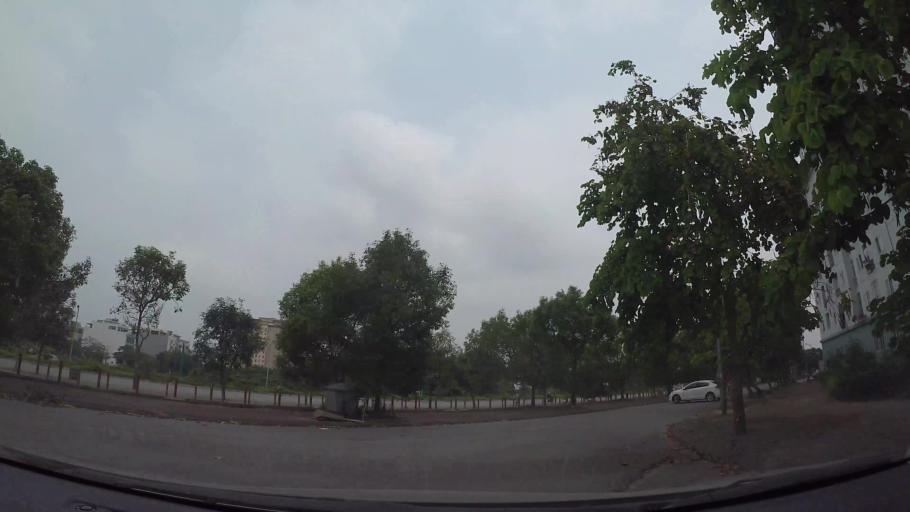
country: VN
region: Ha Noi
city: Trau Quy
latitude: 21.0579
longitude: 105.9135
